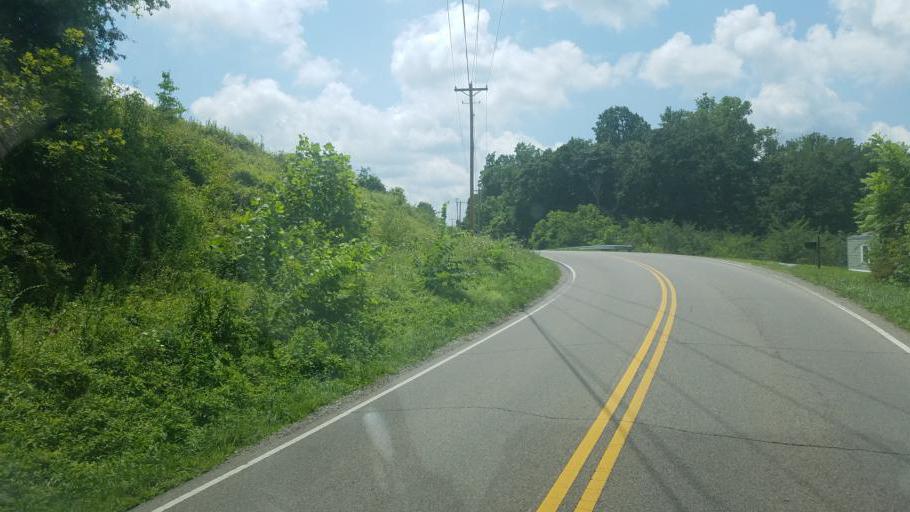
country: US
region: Ohio
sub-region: Ross County
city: Chillicothe
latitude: 39.2538
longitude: -82.7923
